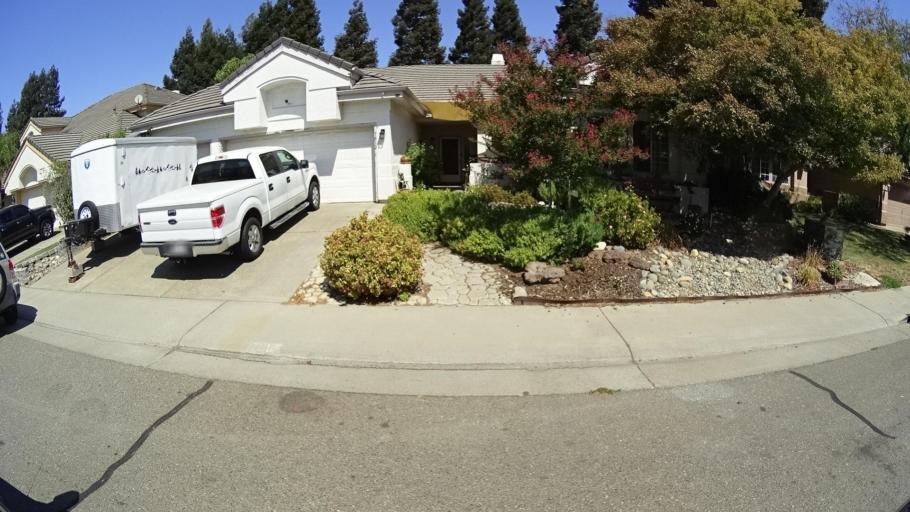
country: US
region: California
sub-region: Sacramento County
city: Laguna
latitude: 38.4147
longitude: -121.4122
